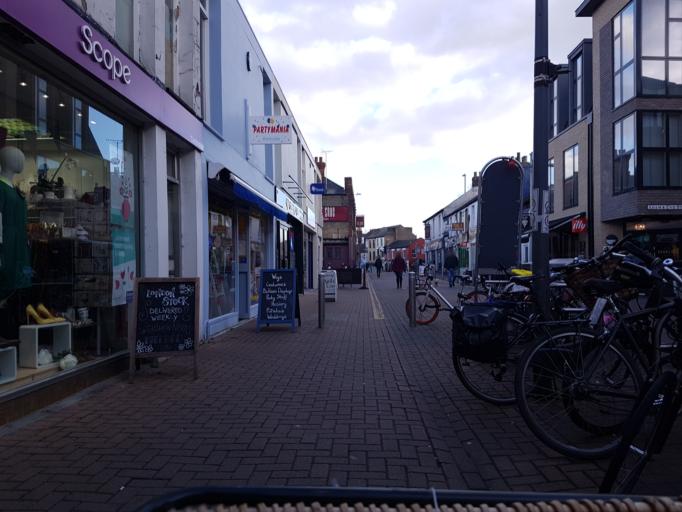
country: GB
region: England
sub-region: Cambridgeshire
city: Cambridge
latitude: 52.2054
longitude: 0.1328
